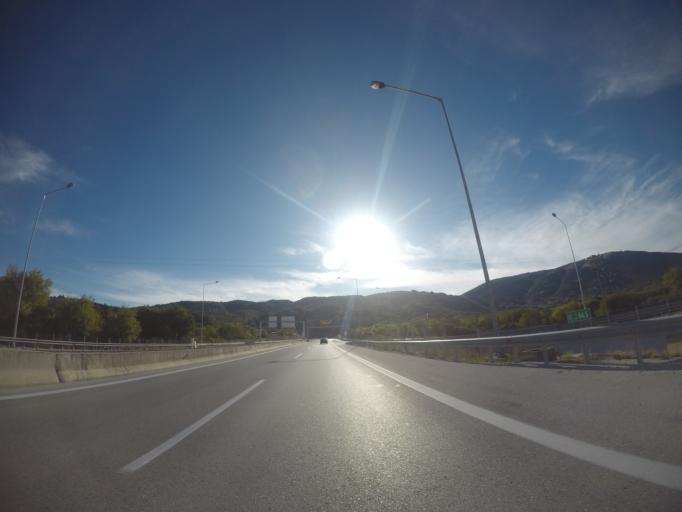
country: GR
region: Epirus
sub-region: Nomos Ioanninon
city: Pedini
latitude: 39.5888
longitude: 20.8179
